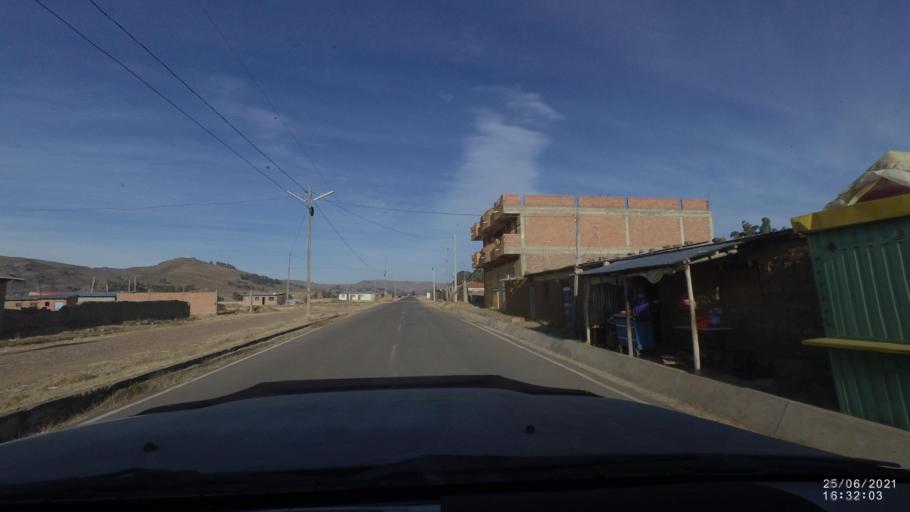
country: BO
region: Cochabamba
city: Arani
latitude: -17.8043
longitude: -65.7990
